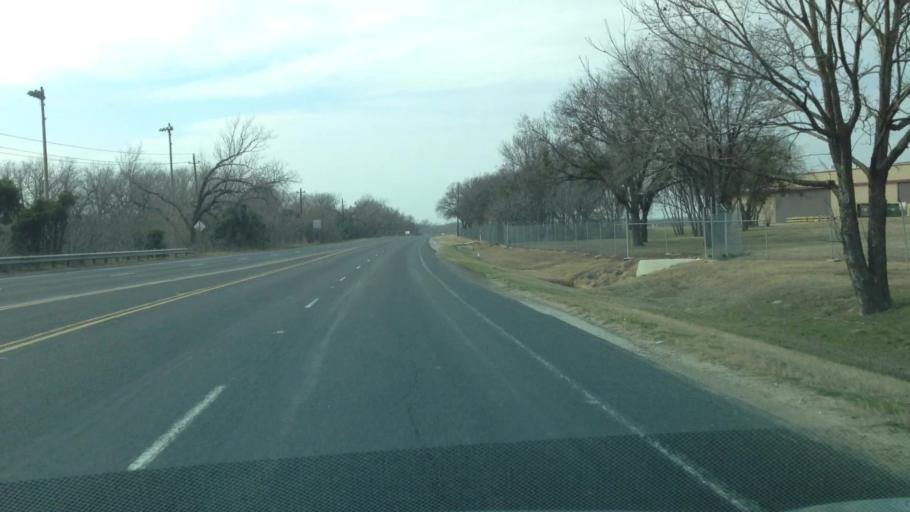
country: US
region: Texas
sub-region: Travis County
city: Garfield
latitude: 30.1736
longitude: -97.6718
